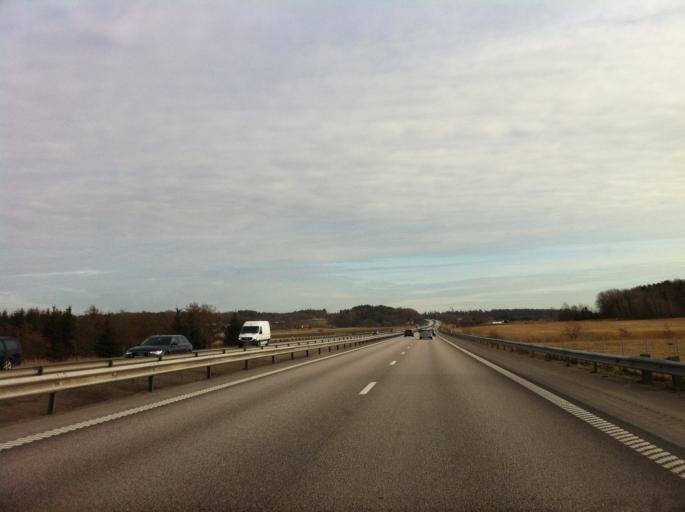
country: SE
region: Vaestra Goetaland
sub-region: Molndal
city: Lindome
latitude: 57.5378
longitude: 12.0514
